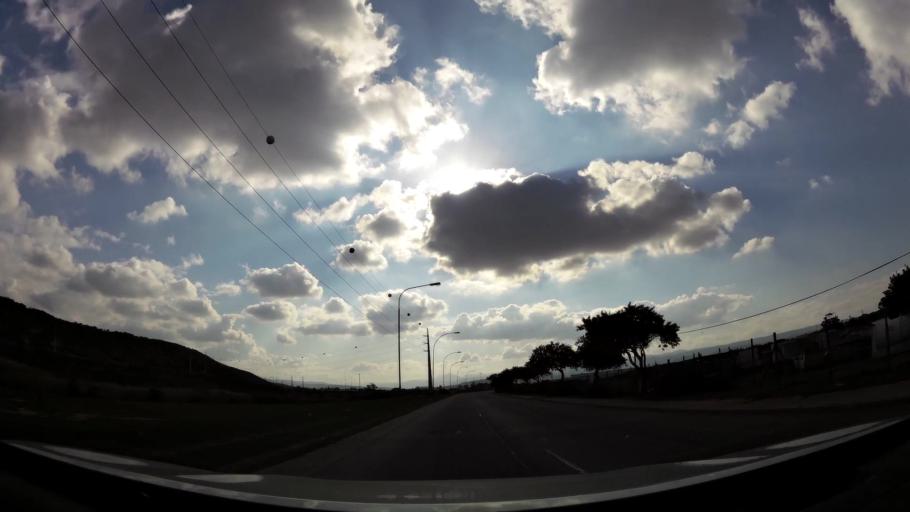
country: ZA
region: Eastern Cape
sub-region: Nelson Mandela Bay Metropolitan Municipality
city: Uitenhage
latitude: -33.7823
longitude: 25.3961
